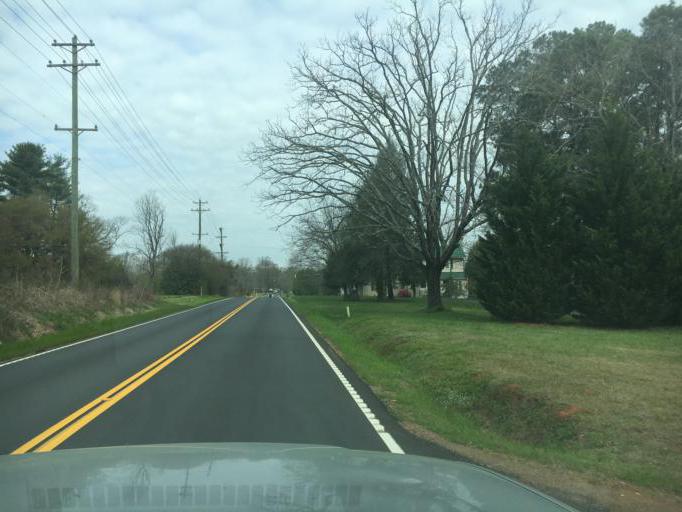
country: US
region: South Carolina
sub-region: Spartanburg County
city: Inman
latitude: 35.0055
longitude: -82.0717
